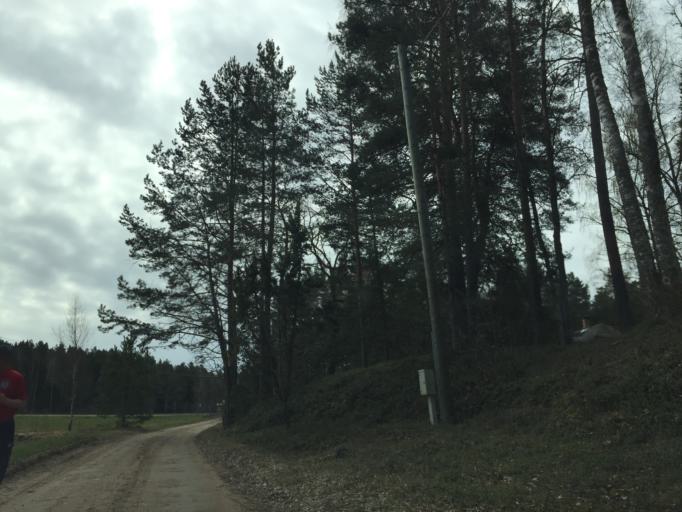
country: LV
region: Salacgrivas
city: Salacgriva
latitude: 57.5344
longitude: 24.3740
